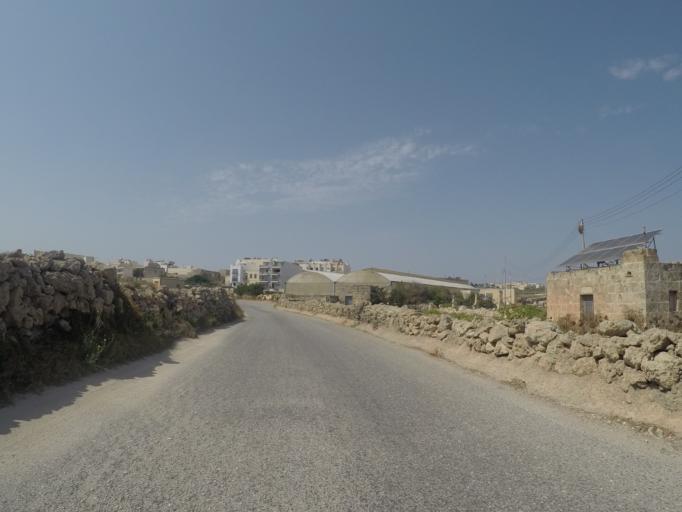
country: MT
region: L-Imgarr
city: Imgarr
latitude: 35.9240
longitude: 14.3792
